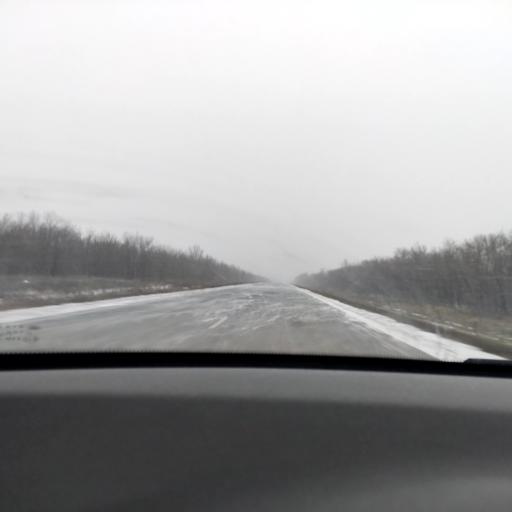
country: RU
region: Samara
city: Novokuybyshevsk
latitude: 52.9351
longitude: 49.9071
